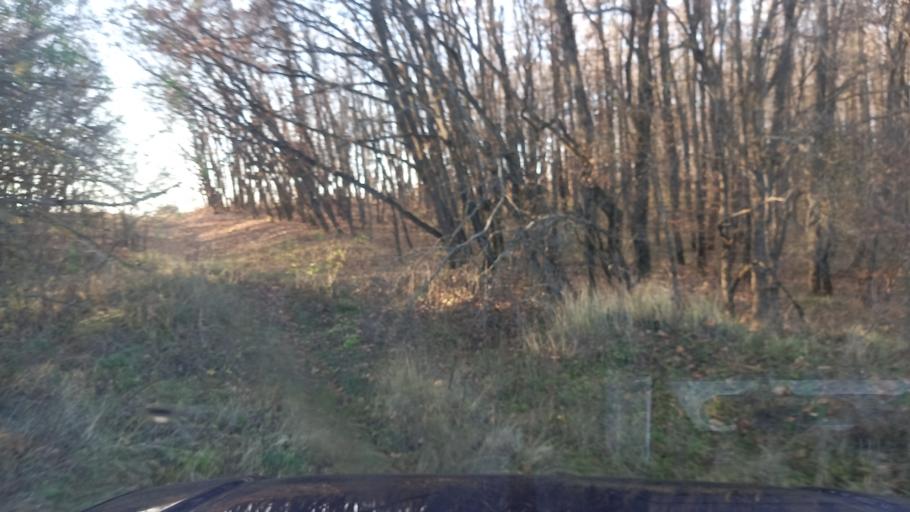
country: RU
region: Krasnodarskiy
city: Azovskaya
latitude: 44.8070
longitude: 38.5910
